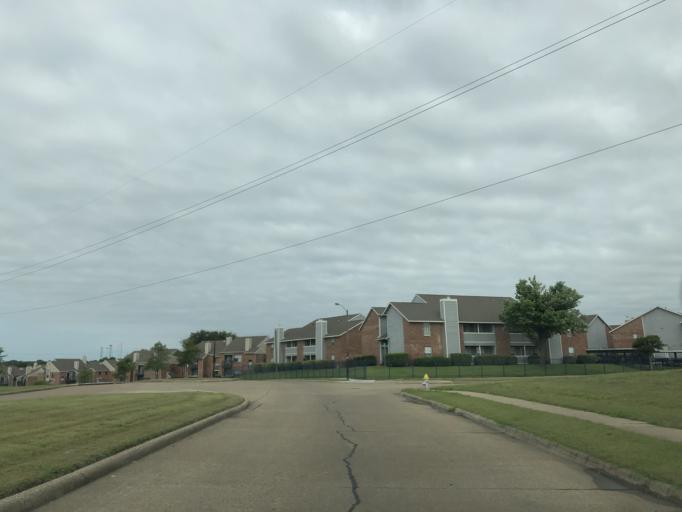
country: US
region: Texas
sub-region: Dallas County
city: Sunnyvale
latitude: 32.8412
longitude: -96.6197
